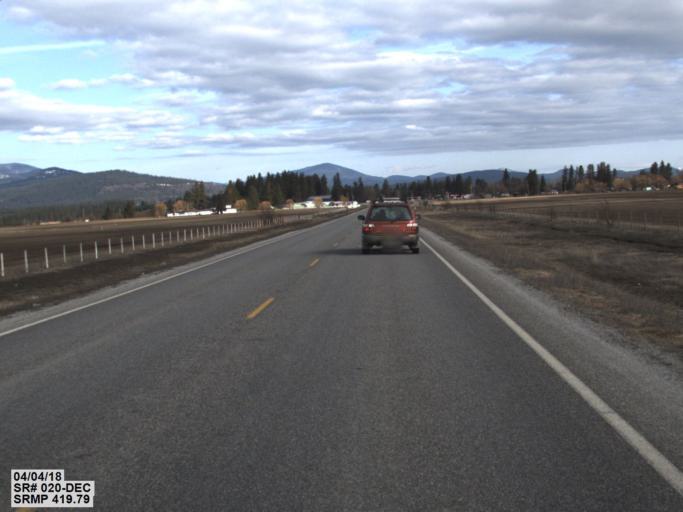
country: US
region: Washington
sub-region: Pend Oreille County
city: Newport
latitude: 48.3269
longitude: -117.2984
